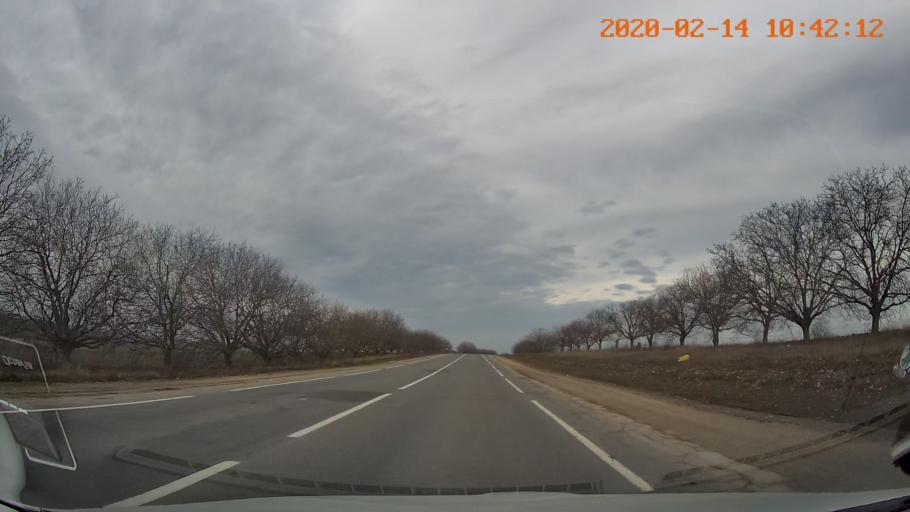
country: MD
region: Riscani
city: Riscani
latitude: 47.9907
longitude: 27.5748
